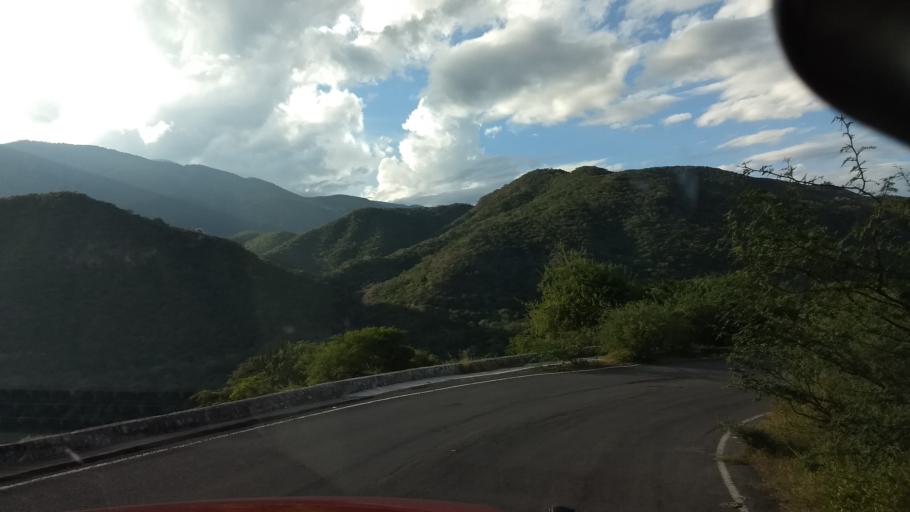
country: MX
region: Colima
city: Suchitlan
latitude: 19.4597
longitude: -103.8276
